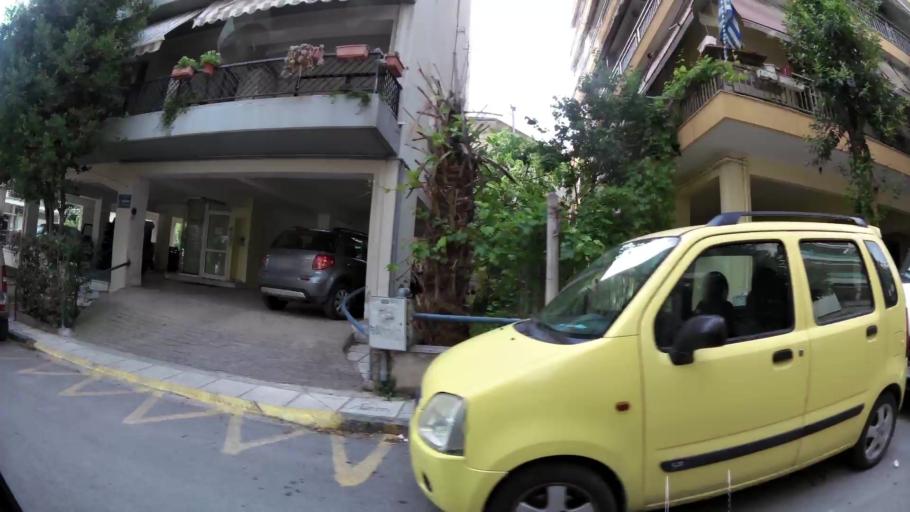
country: GR
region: Central Macedonia
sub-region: Nomos Thessalonikis
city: Kalamaria
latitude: 40.5774
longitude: 22.9519
